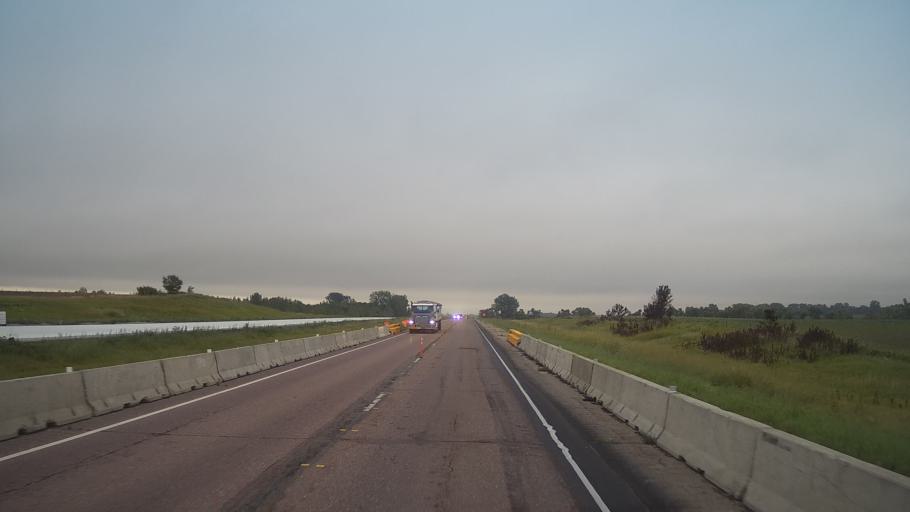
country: US
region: Minnesota
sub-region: Faribault County
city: Winnebago
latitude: 43.6661
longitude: -94.2872
